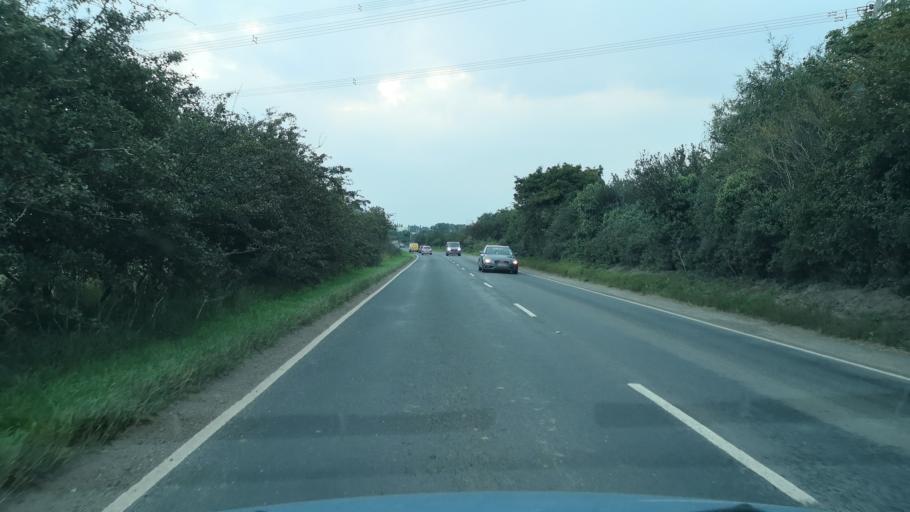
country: GB
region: England
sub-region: East Riding of Yorkshire
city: Snaith
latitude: 53.6852
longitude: -1.0499
